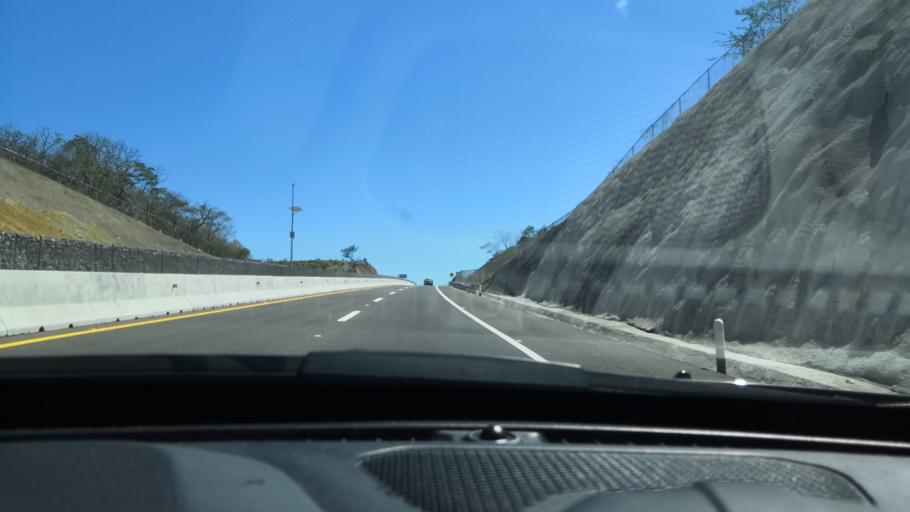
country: MX
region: Nayarit
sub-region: Compostela
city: Juan Escutia (Borbollon)
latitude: 21.1219
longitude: -104.8894
